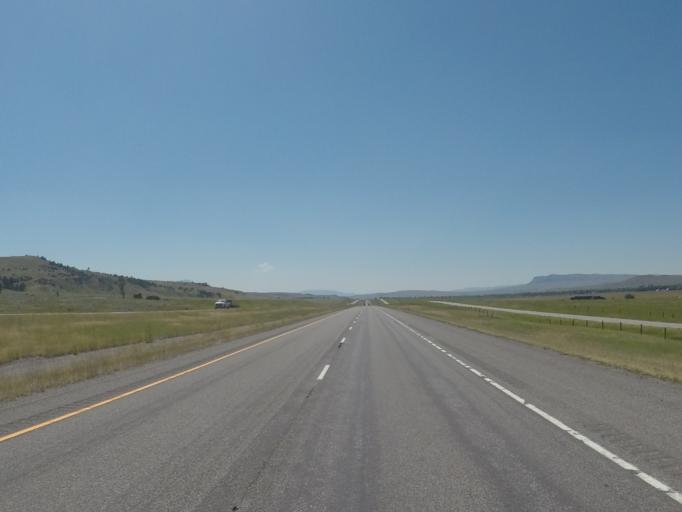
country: US
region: Montana
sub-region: Sweet Grass County
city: Big Timber
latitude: 45.7651
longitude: -110.0942
